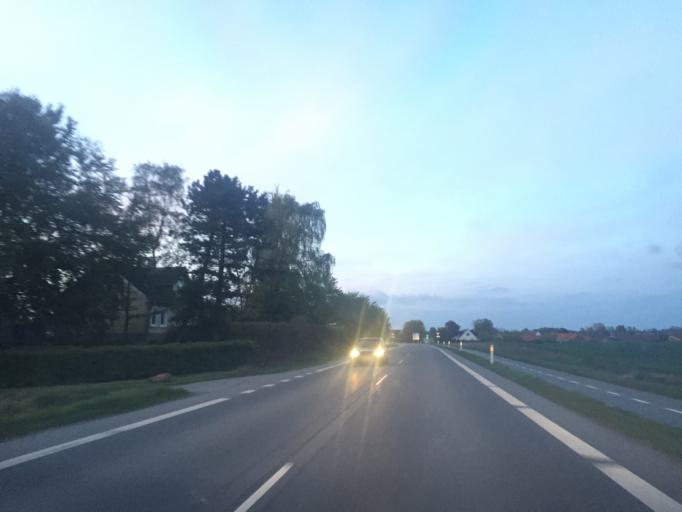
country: DK
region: South Denmark
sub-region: Nyborg Kommune
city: Nyborg
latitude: 55.3023
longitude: 10.7223
